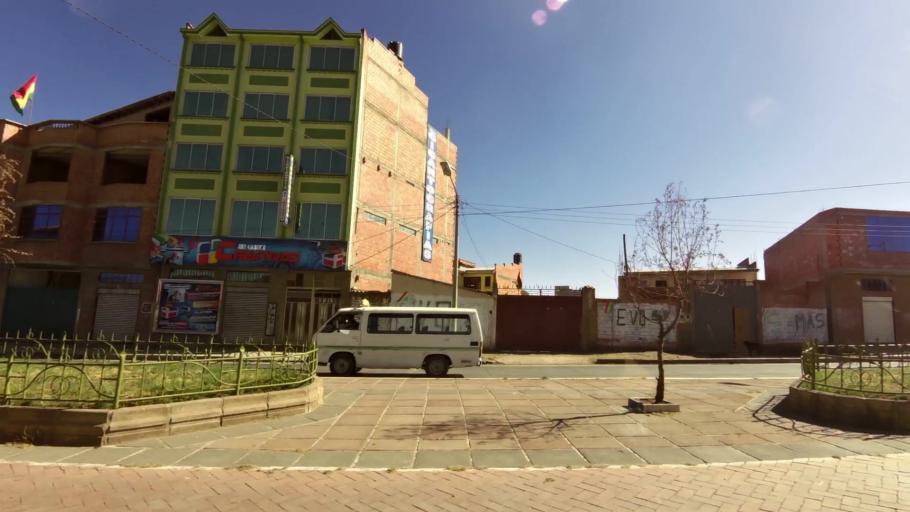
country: BO
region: La Paz
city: La Paz
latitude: -16.5169
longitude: -68.1811
